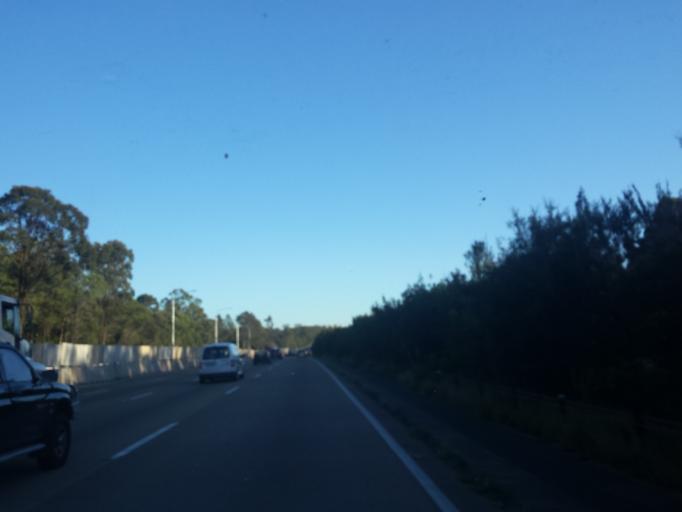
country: AU
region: Queensland
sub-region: Gold Coast
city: Oxenford
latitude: -27.8491
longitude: 153.3065
